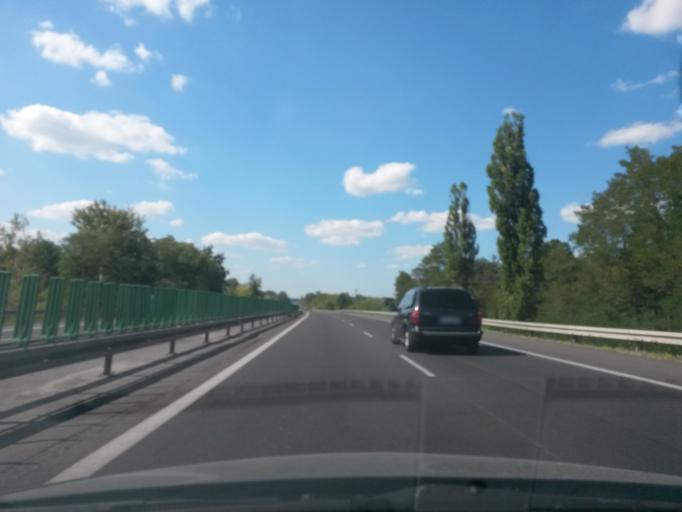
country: PL
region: Masovian Voivodeship
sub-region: Powiat nowodworski
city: Nowy Dwor Mazowiecki
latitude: 52.3939
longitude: 20.7202
